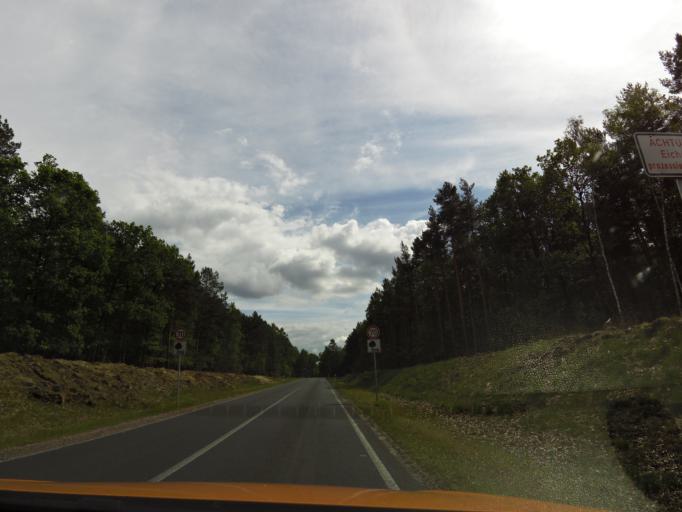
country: DE
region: Brandenburg
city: Michendorf
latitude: 52.3019
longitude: 12.9741
